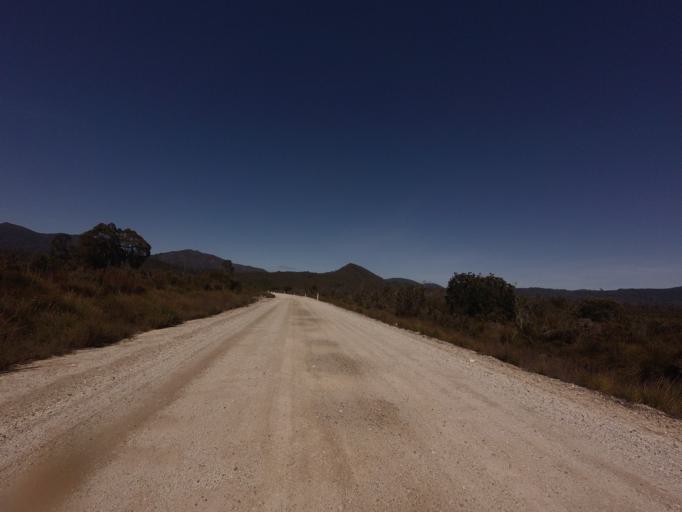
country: AU
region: Tasmania
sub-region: Huon Valley
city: Geeveston
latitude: -42.8930
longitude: 146.3746
